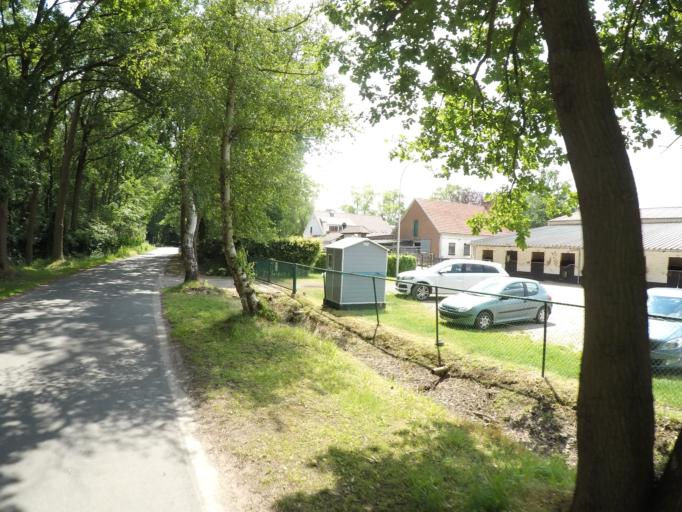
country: BE
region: Flanders
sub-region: Provincie Antwerpen
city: Schilde
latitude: 51.2625
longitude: 4.6000
